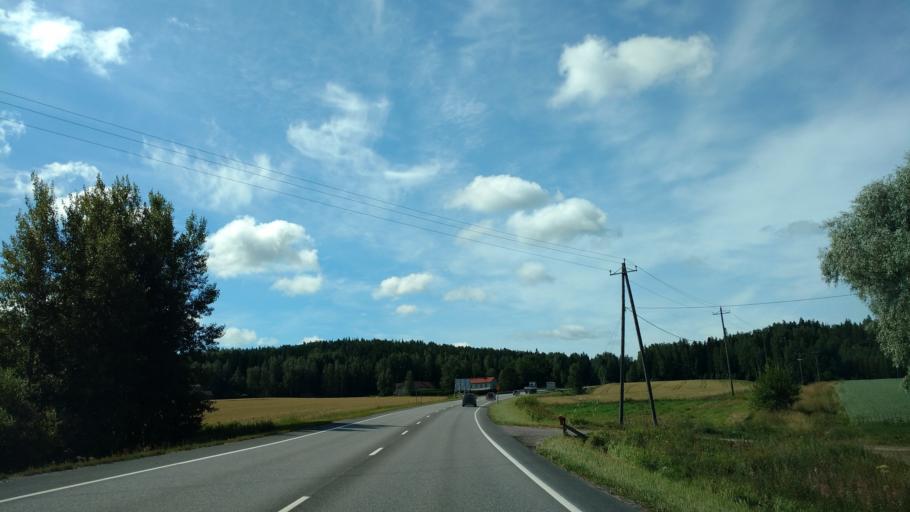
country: FI
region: Varsinais-Suomi
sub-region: Salo
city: Salo
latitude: 60.3497
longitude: 23.1414
